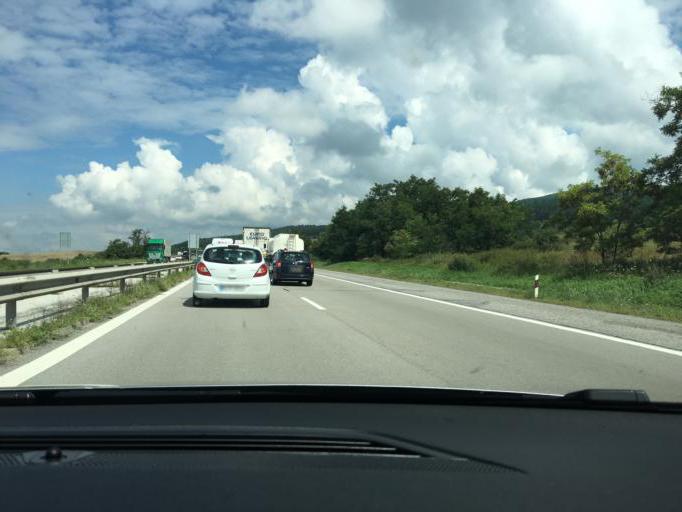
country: BG
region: Sofiya
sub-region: Obshtina Ikhtiman
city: Ikhtiman
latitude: 42.4168
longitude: 23.8594
